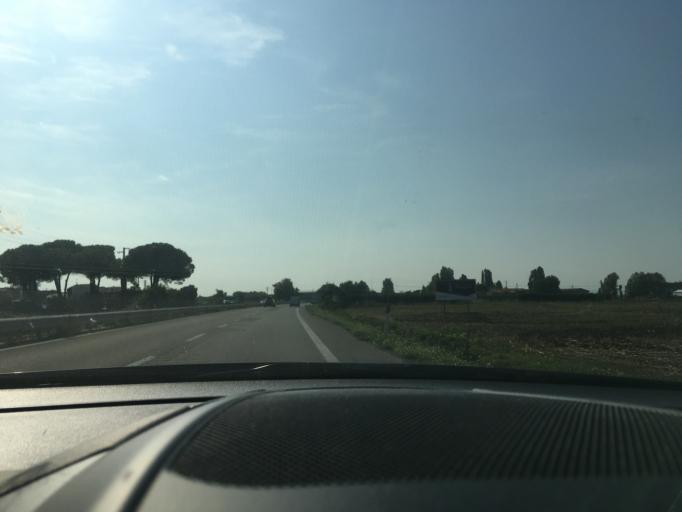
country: IT
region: Emilia-Romagna
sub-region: Provincia di Rimini
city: Bellaria-Igea Marina
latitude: 44.1284
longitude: 12.4685
